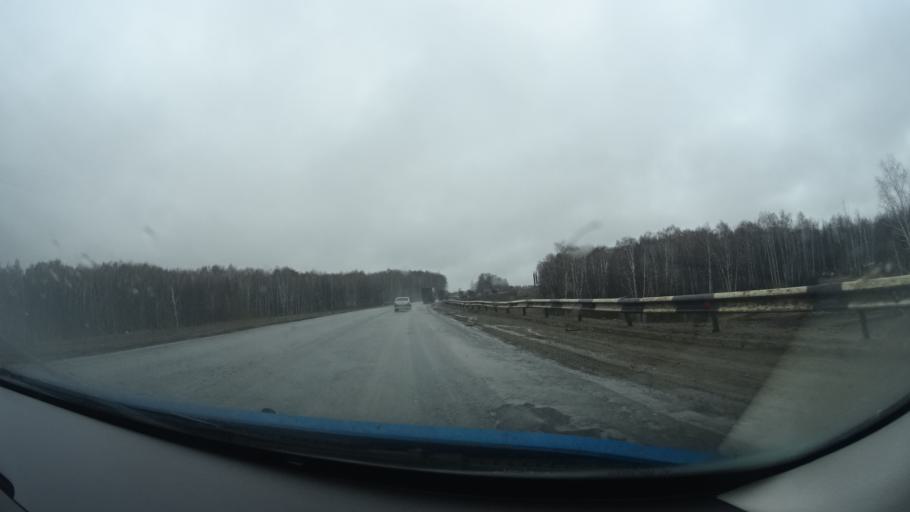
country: RU
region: Bashkortostan
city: Kandry
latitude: 54.5938
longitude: 54.2806
